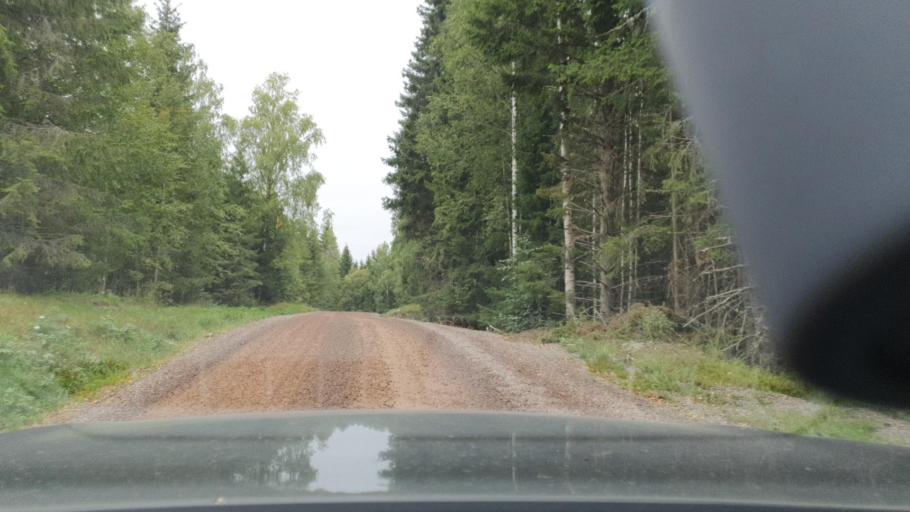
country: SE
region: Vaermland
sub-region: Arvika Kommun
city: Arvika
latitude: 59.9678
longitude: 12.6602
